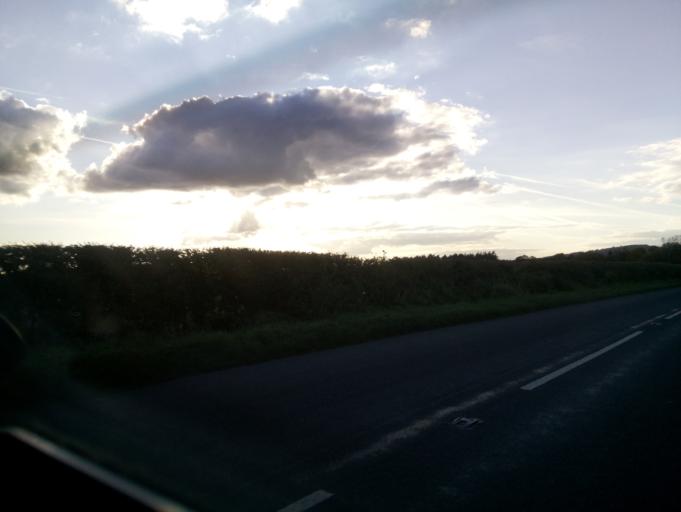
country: GB
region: England
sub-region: Worcestershire
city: Upton upon Severn
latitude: 52.0112
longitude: -2.2831
